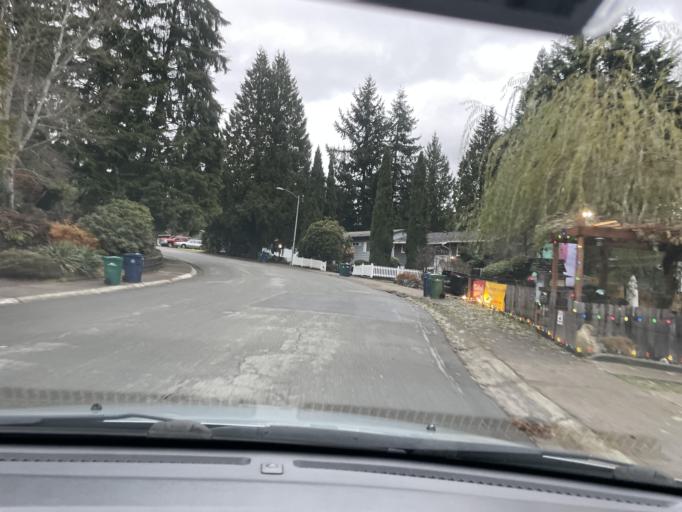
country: US
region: Washington
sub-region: King County
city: Kingsgate
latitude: 47.7211
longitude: -122.1793
